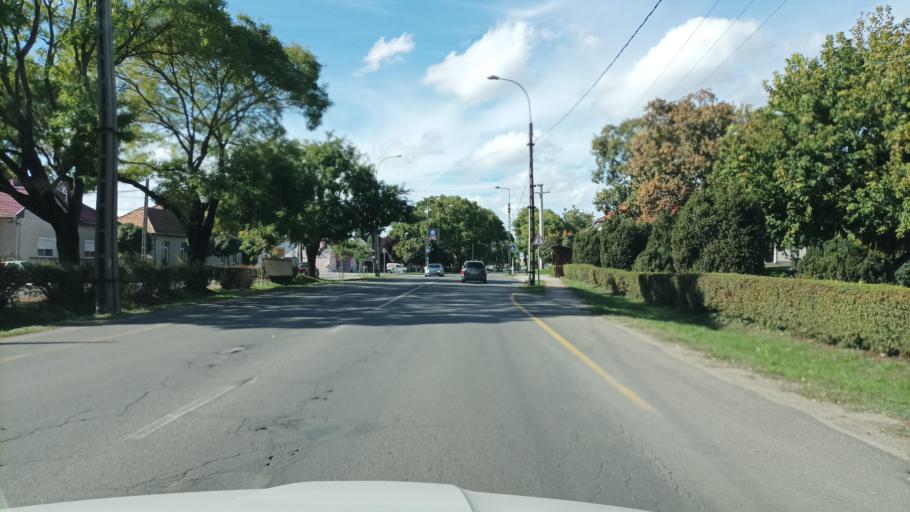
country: HU
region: Pest
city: Vecses
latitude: 47.4068
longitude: 19.2822
